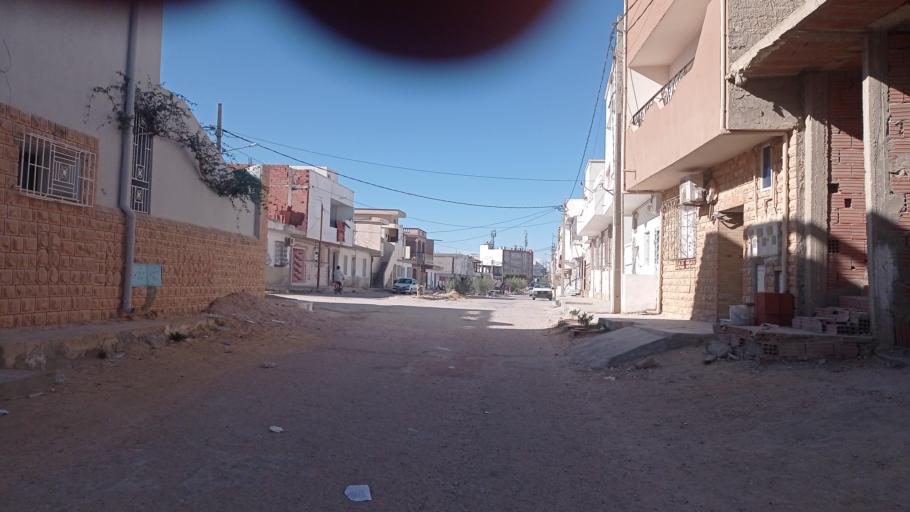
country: TN
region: Qabis
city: Gabes
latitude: 33.8433
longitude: 10.1155
